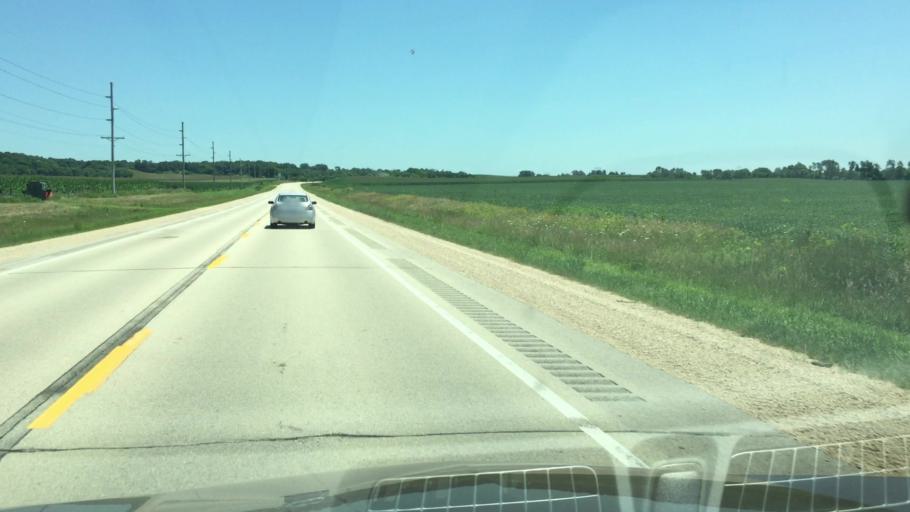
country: US
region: Iowa
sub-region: Jackson County
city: Maquoketa
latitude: 42.0660
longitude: -90.7746
